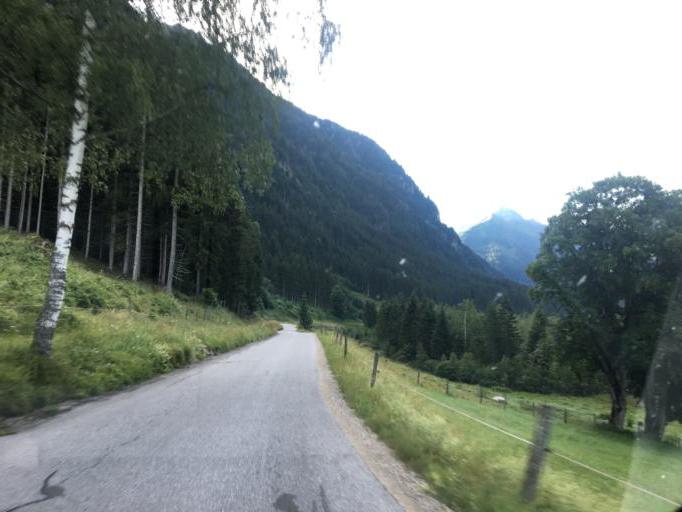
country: AT
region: Styria
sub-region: Politischer Bezirk Liezen
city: Schladming
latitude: 47.3554
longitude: 13.7173
